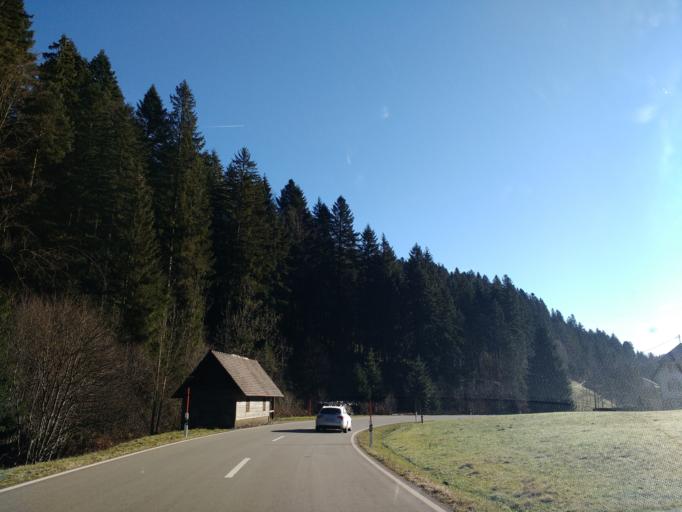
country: DE
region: Baden-Wuerttemberg
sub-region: Karlsruhe Region
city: Bad Rippoldsau-Schapbach
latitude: 48.4431
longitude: 8.3129
